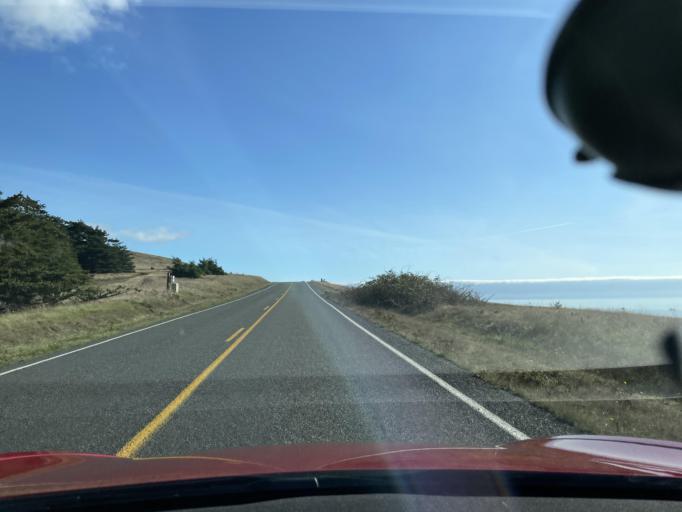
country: US
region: Washington
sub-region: San Juan County
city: Friday Harbor
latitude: 48.4591
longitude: -122.9943
